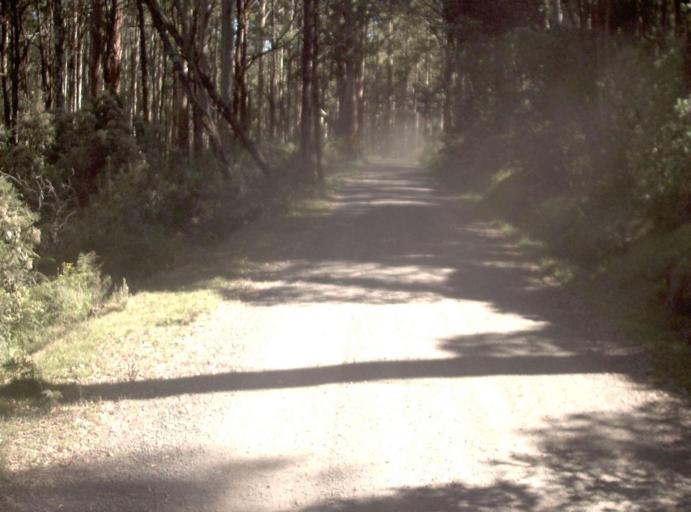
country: AU
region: Victoria
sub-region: Yarra Ranges
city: Millgrove
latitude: -37.7135
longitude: 145.6185
